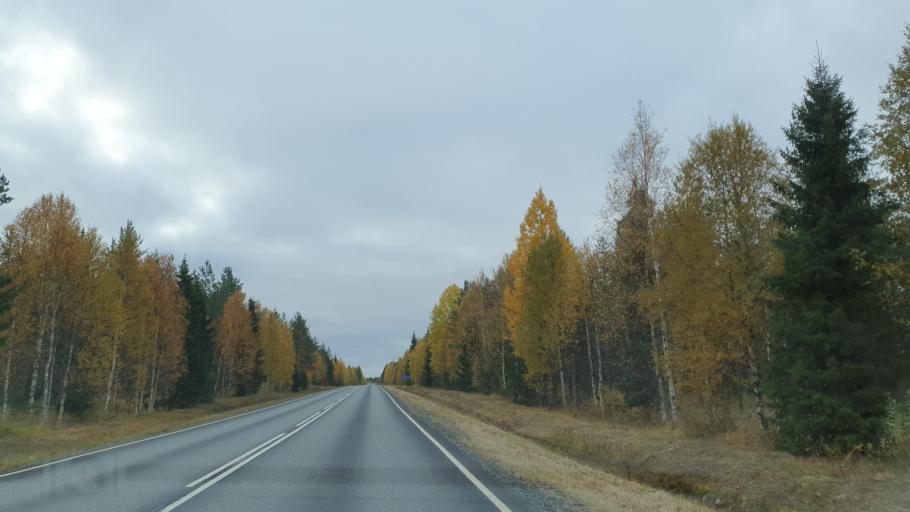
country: FI
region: Lapland
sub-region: Rovaniemi
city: Ranua
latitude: 65.8449
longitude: 26.5414
